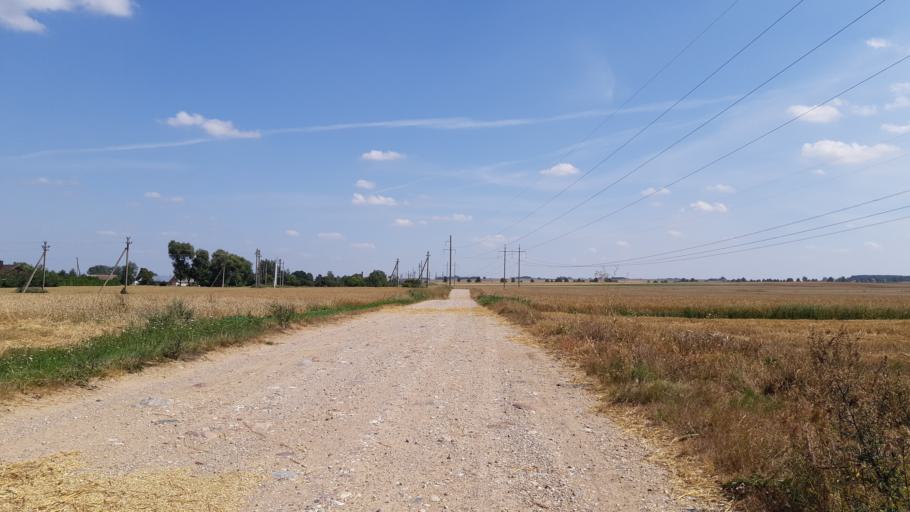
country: LT
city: Virbalis
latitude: 54.6191
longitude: 22.8089
